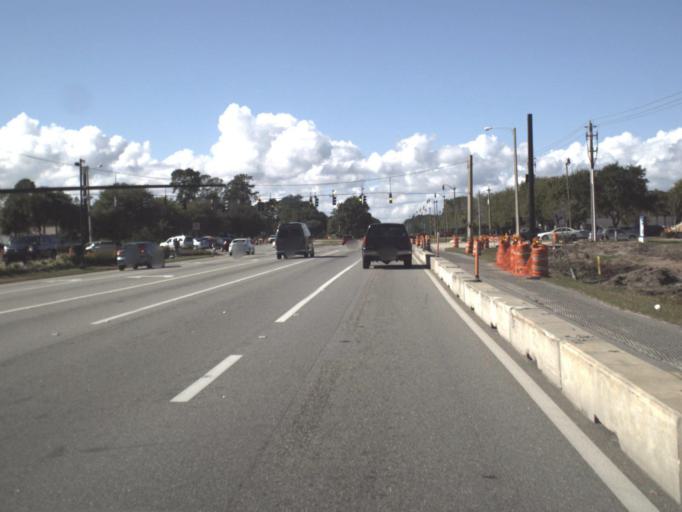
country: US
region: Florida
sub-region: Flagler County
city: Palm Coast
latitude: 29.5536
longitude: -81.2252
